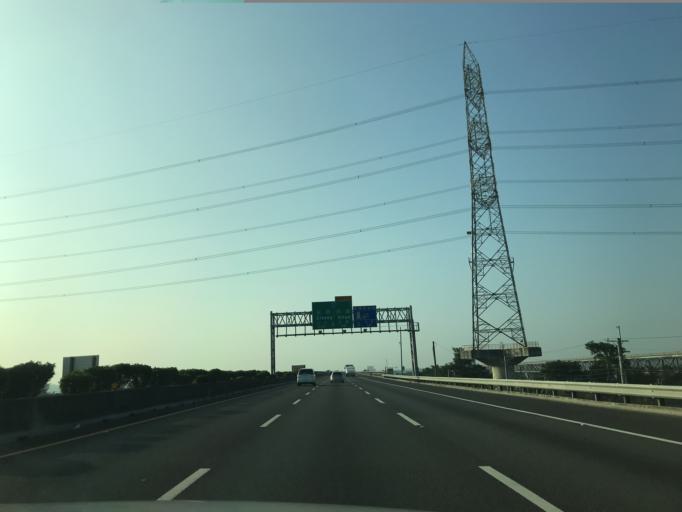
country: TW
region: Taiwan
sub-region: Yunlin
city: Douliu
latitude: 23.8184
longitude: 120.4852
